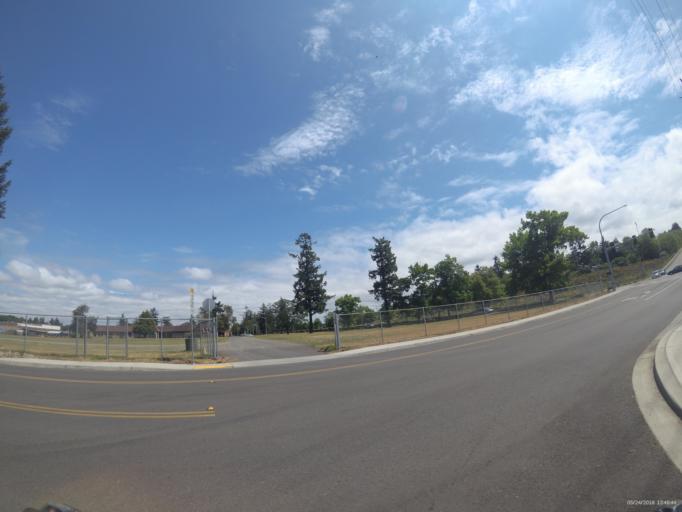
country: US
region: Washington
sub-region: Pierce County
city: Steilacoom
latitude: 47.1773
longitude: -122.5745
